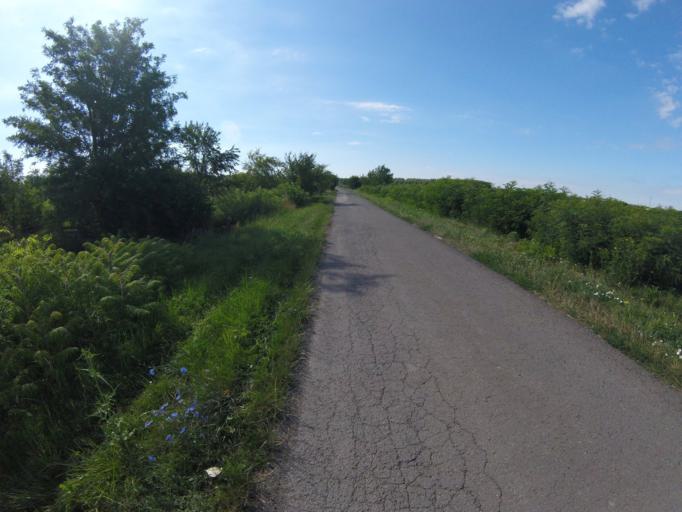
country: HU
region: Heves
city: Tiszanana
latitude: 47.5789
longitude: 20.6046
